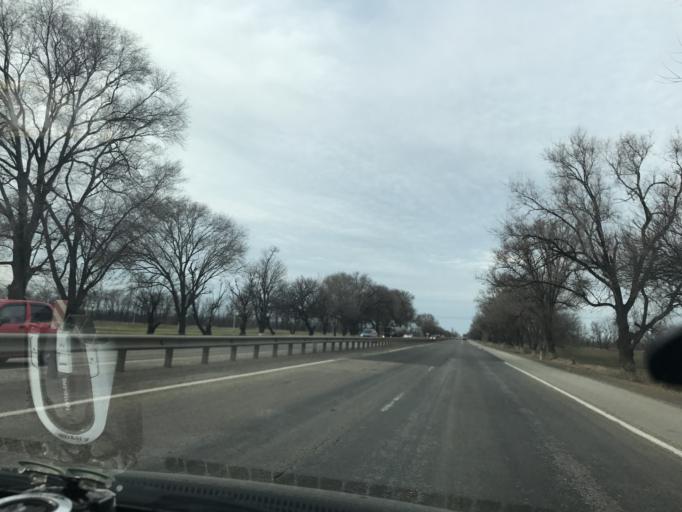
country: RU
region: Krasnodarskiy
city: Novokubansk
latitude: 45.0403
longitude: 41.0011
